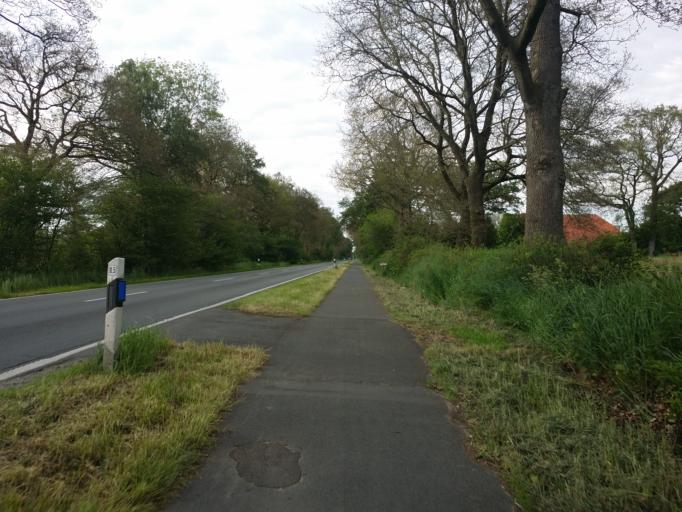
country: DE
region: Lower Saxony
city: Wittmund
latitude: 53.5339
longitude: 7.7819
